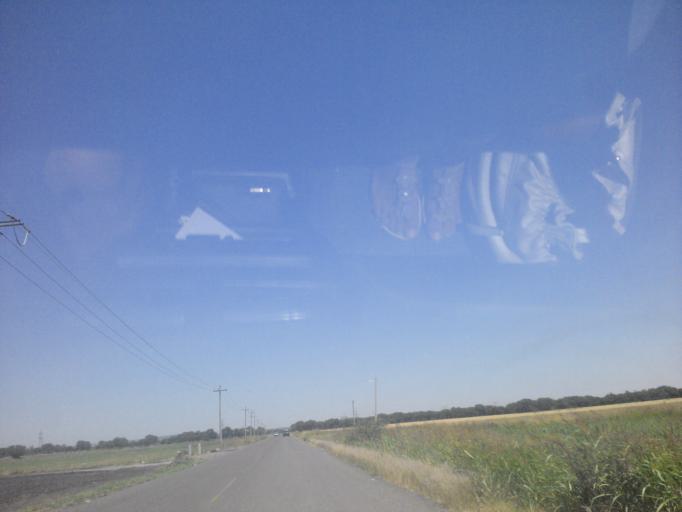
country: MX
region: Guanajuato
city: San Roque
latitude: 20.9547
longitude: -101.8933
